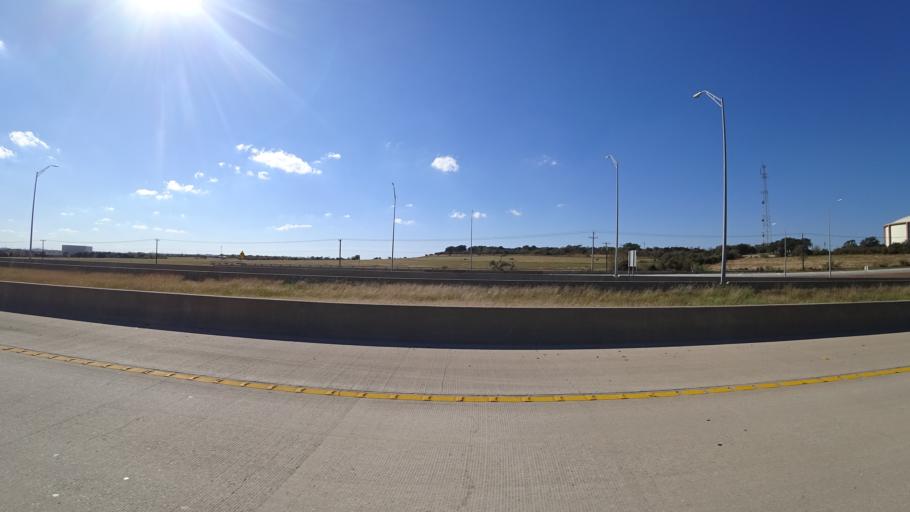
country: US
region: Texas
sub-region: Travis County
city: Wells Branch
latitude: 30.4567
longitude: -97.6975
